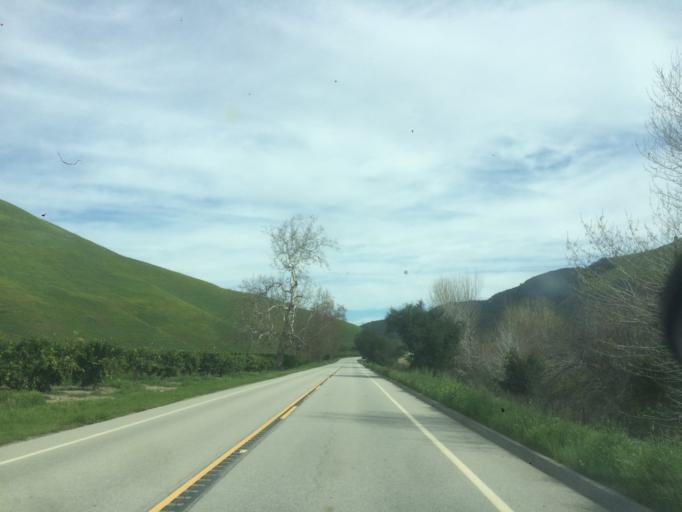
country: US
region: California
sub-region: San Luis Obispo County
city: Arroyo Grande
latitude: 35.1824
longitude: -120.5099
